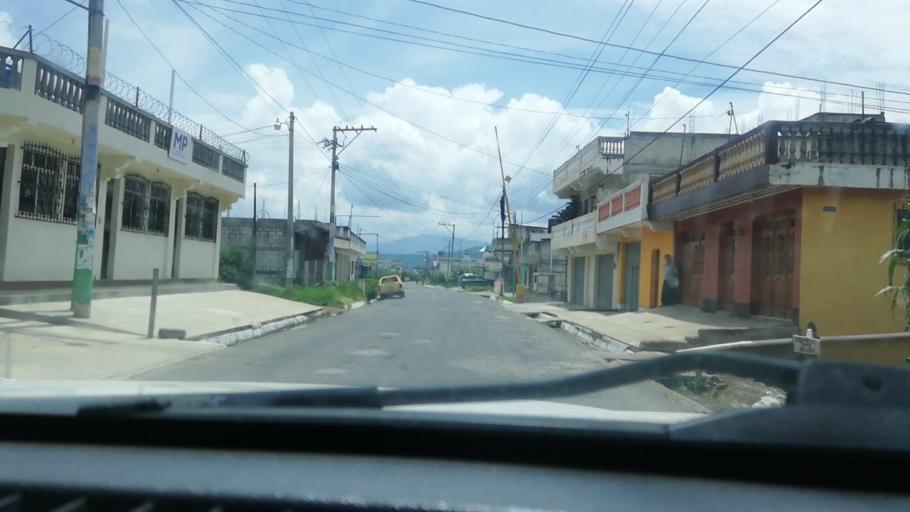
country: GT
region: Totonicapan
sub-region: Municipio de San Andres Xecul
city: San Andres Xecul
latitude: 14.9050
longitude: -91.4759
